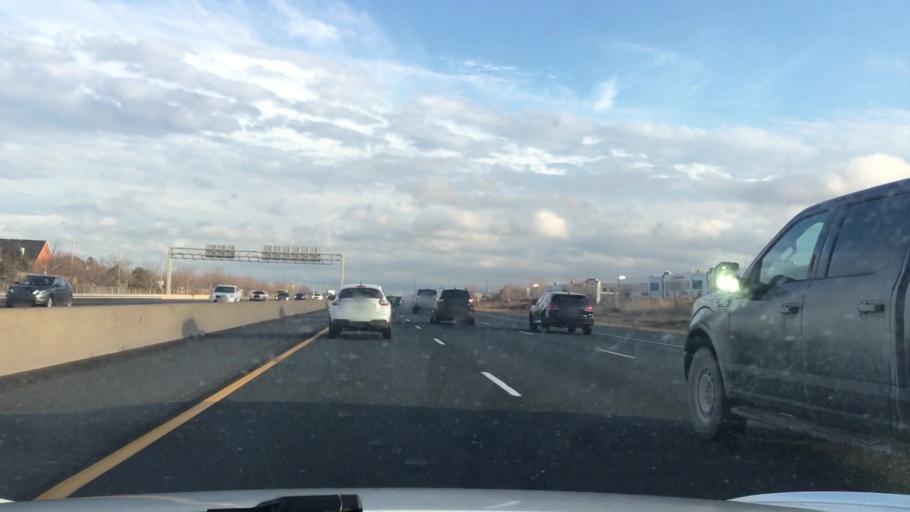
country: CA
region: Ontario
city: Hamilton
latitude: 43.2305
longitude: -79.6924
